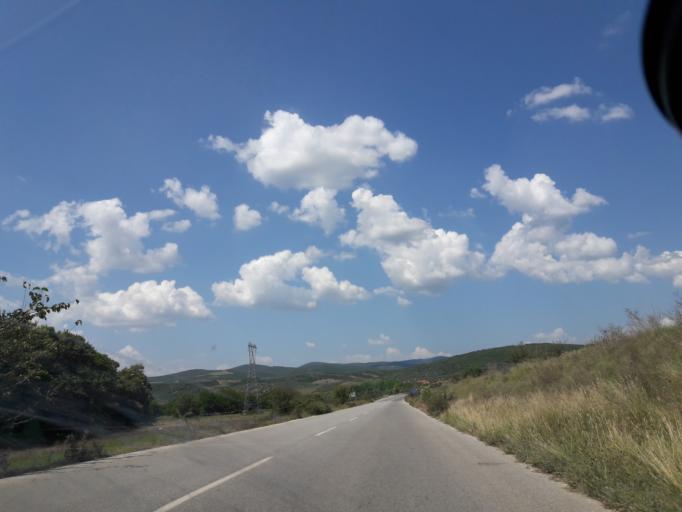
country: GR
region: Central Macedonia
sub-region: Nomos Chalkidikis
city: Megali Panagia
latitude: 40.3705
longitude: 23.6482
